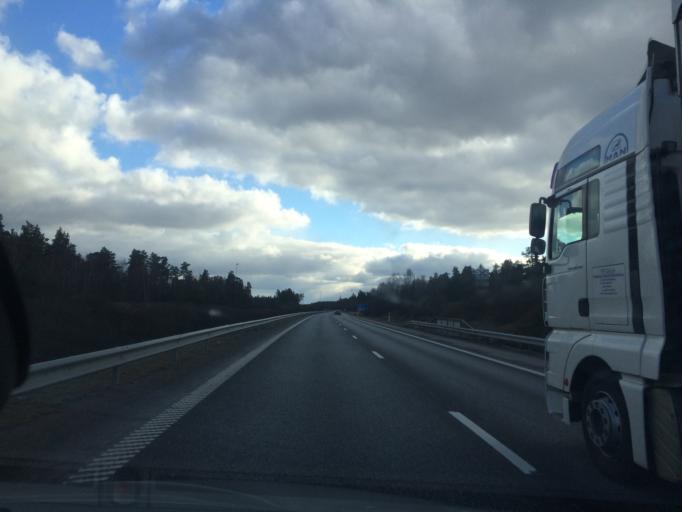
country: SE
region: Joenkoeping
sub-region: Vaggeryds Kommun
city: Skillingaryd
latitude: 57.3523
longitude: 14.1050
